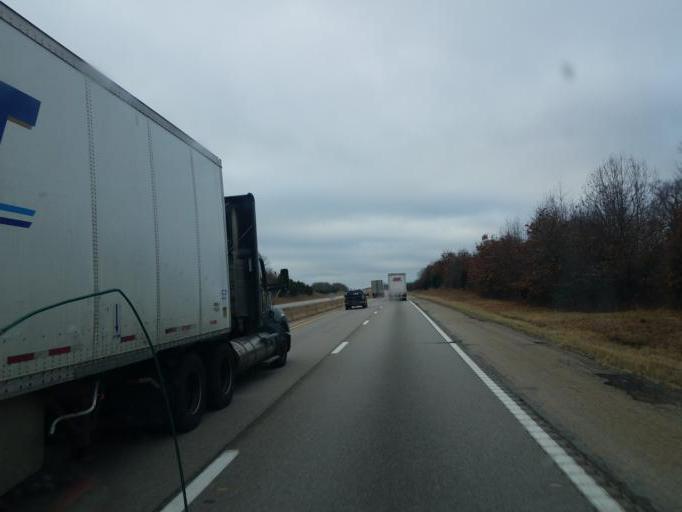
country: US
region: Missouri
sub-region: Laclede County
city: Lebanon
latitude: 37.5471
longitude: -92.8092
